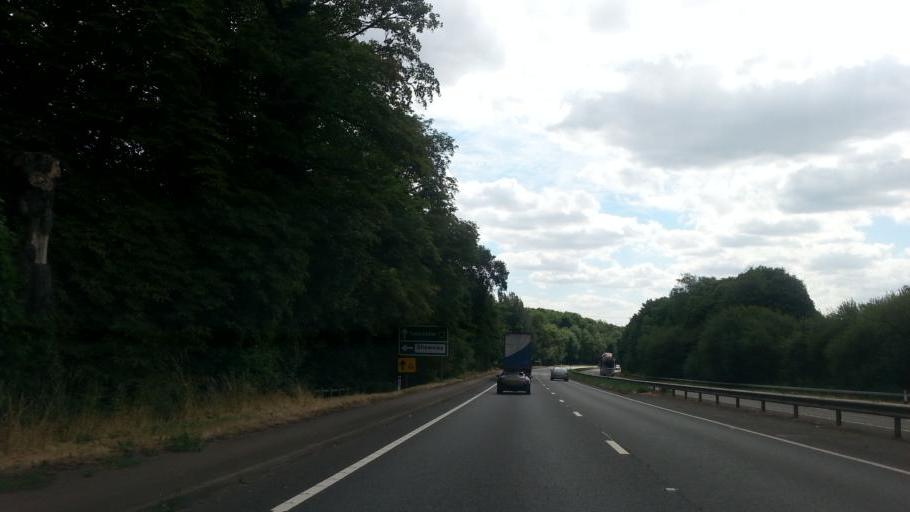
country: GB
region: England
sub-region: Northamptonshire
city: Blisworth
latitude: 52.1549
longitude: -0.9663
